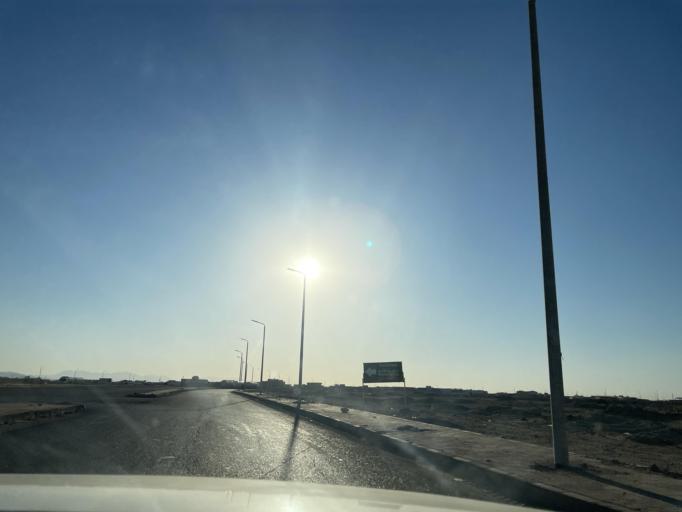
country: EG
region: Red Sea
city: Hurghada
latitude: 27.2188
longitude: 33.7895
